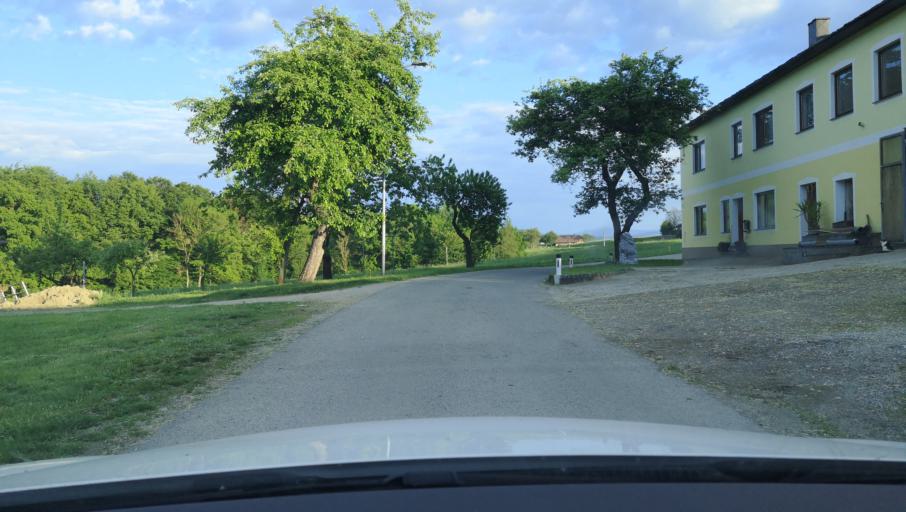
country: AT
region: Lower Austria
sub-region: Politischer Bezirk Melk
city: Blindenmarkt
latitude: 48.1401
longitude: 14.9913
